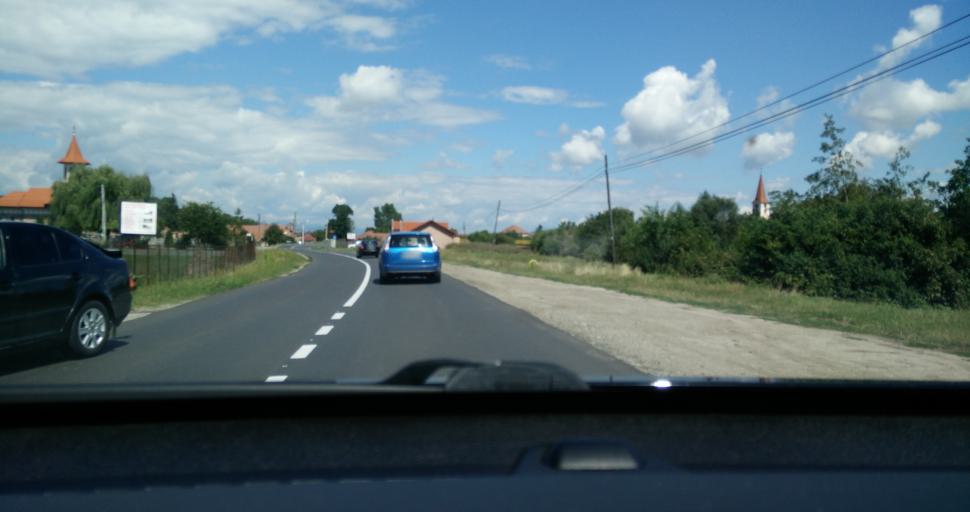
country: RO
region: Alba
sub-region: Municipiul Sebes
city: Petresti
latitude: 45.9170
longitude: 23.5558
